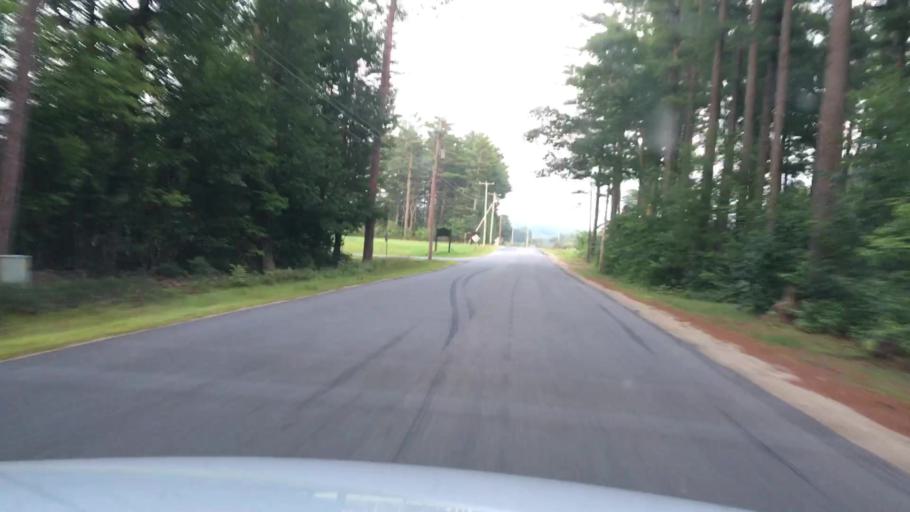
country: US
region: Maine
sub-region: Oxford County
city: Bethel
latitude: 44.4208
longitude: -70.8094
